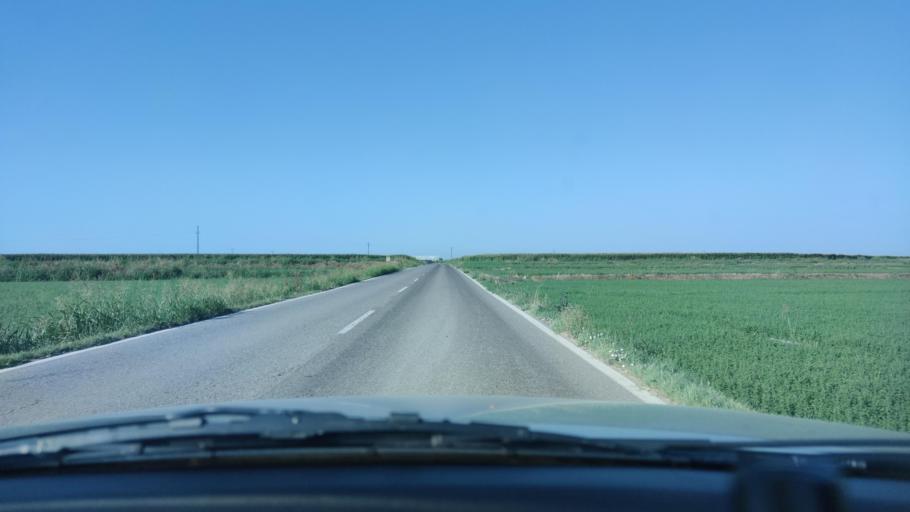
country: ES
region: Catalonia
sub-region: Provincia de Lleida
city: Bellvis
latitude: 41.6464
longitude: 0.7975
